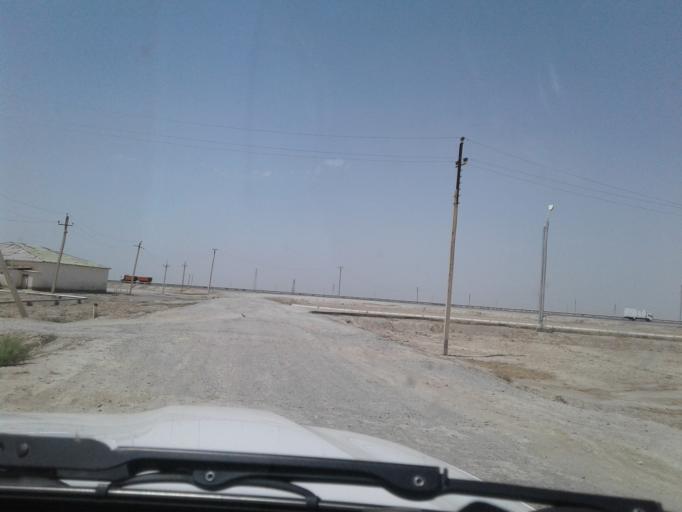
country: IR
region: Razavi Khorasan
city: Kalat-e Naderi
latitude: 37.2054
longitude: 60.0231
